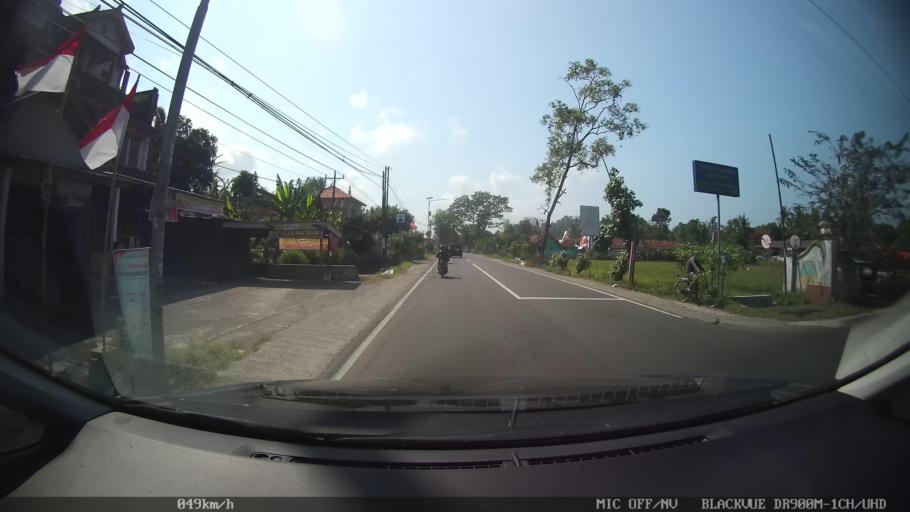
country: ID
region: Daerah Istimewa Yogyakarta
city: Srandakan
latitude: -7.9309
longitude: 110.2096
